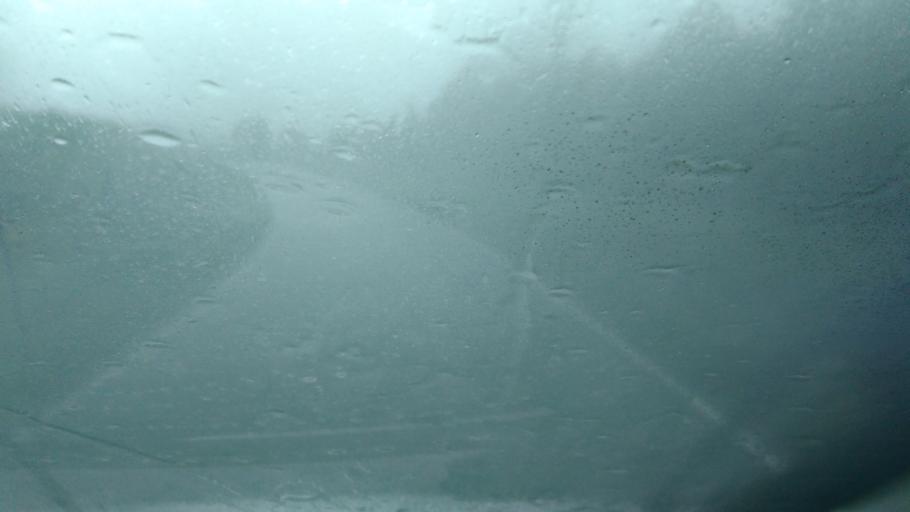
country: US
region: Kentucky
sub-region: Fleming County
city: Flemingsburg
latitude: 38.4959
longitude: -83.5661
